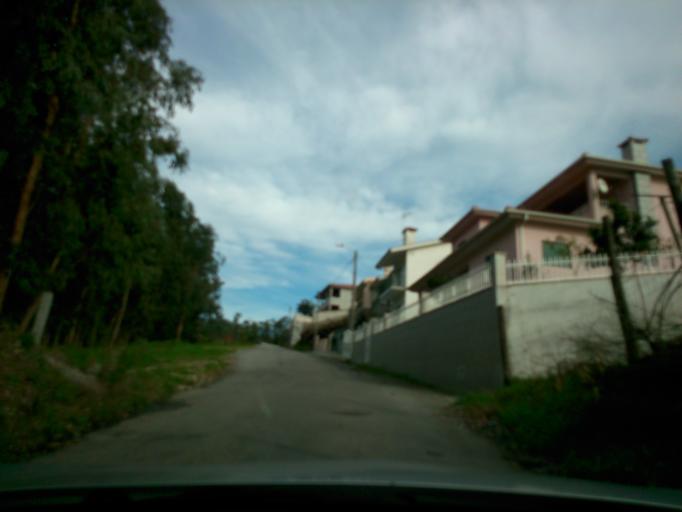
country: PT
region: Porto
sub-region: Amarante
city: Figueiro
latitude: 41.2929
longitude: -8.1988
